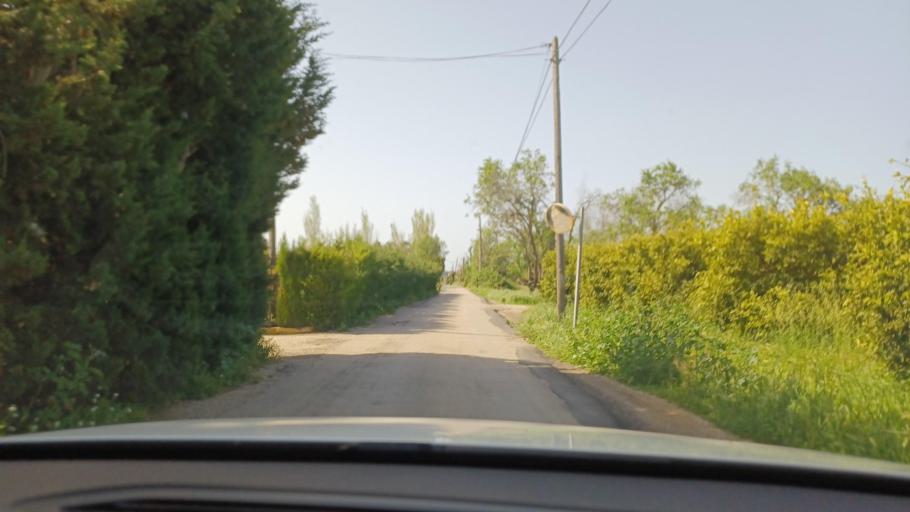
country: ES
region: Catalonia
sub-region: Provincia de Tarragona
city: Tortosa
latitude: 40.7943
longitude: 0.5155
